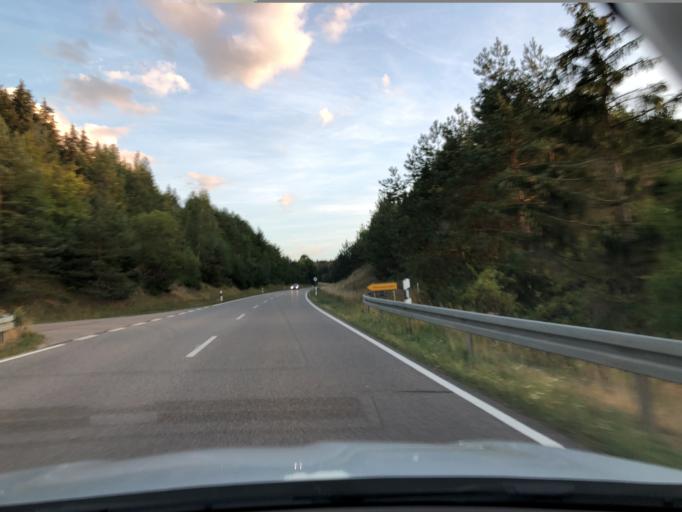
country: DE
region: Bavaria
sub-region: Upper Palatinate
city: Illschwang
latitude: 49.4691
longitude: 11.7041
